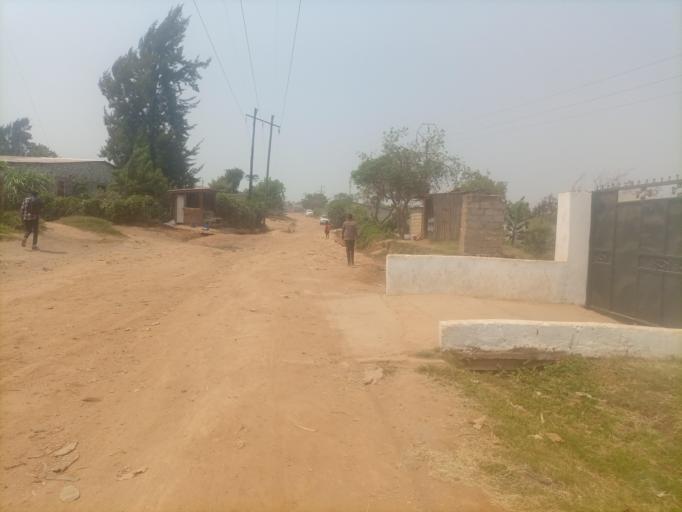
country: ZM
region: Lusaka
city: Lusaka
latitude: -15.3948
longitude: 28.3679
